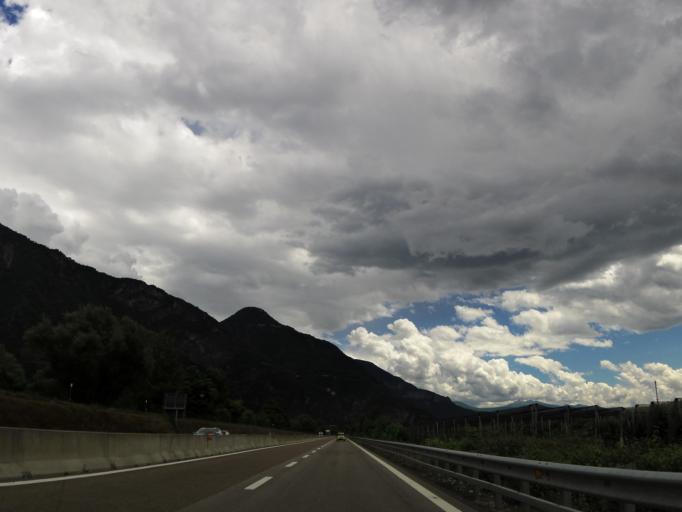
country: IT
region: Trentino-Alto Adige
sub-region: Bolzano
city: Gargazzone
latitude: 46.5702
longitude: 11.2047
